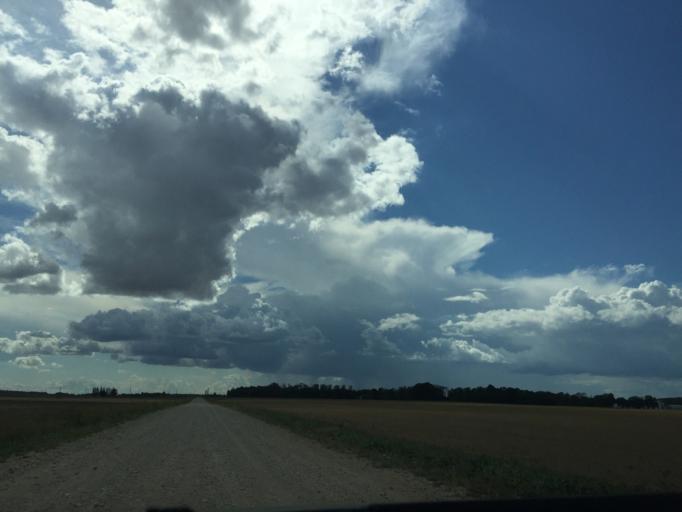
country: LT
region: Siauliu apskritis
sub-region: Joniskis
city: Joniskis
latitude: 56.3413
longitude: 23.6085
